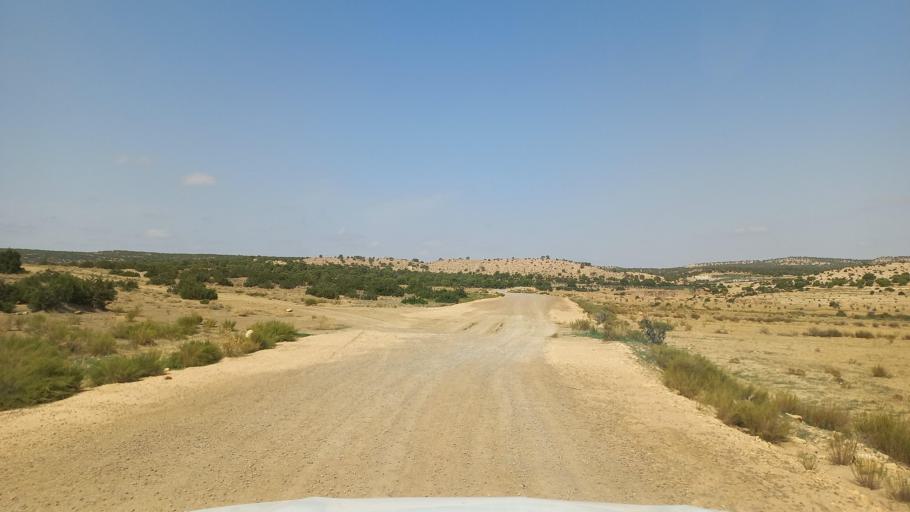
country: TN
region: Al Qasrayn
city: Sbiba
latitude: 35.3897
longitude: 8.9543
